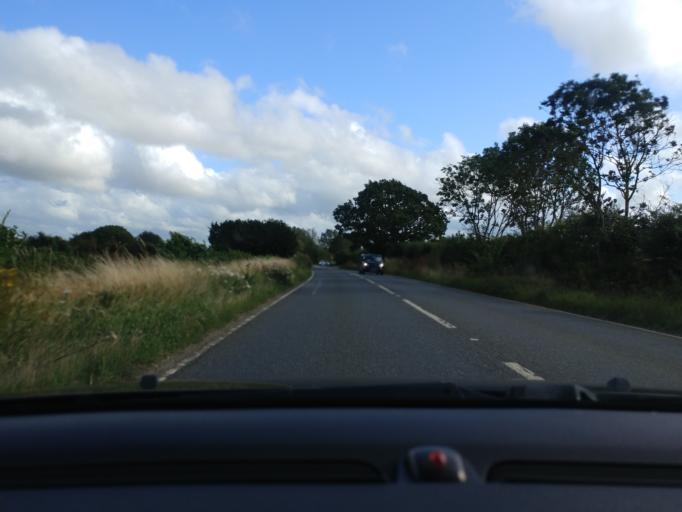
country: GB
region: England
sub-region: Oxfordshire
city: Kidlington
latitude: 51.8703
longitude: -1.2278
